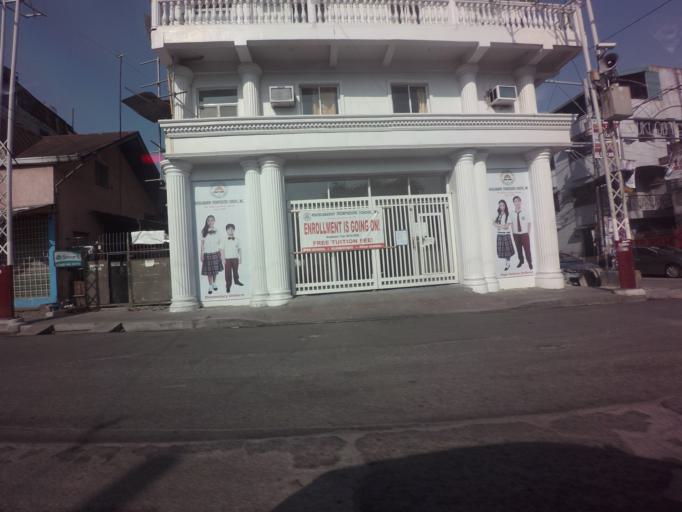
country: PH
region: Calabarzon
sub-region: Province of Rizal
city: Taguig
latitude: 14.4993
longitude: 121.0499
